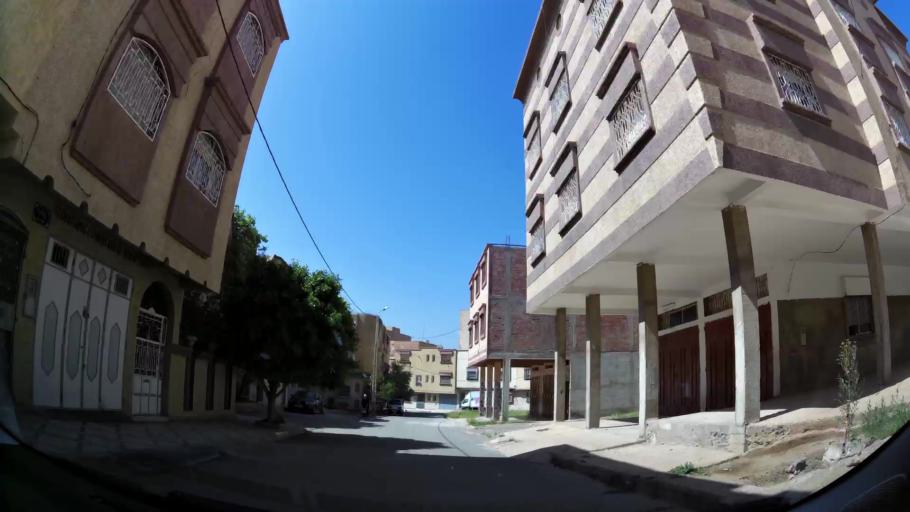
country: MA
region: Oriental
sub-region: Oujda-Angad
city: Oujda
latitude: 34.6739
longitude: -1.9402
